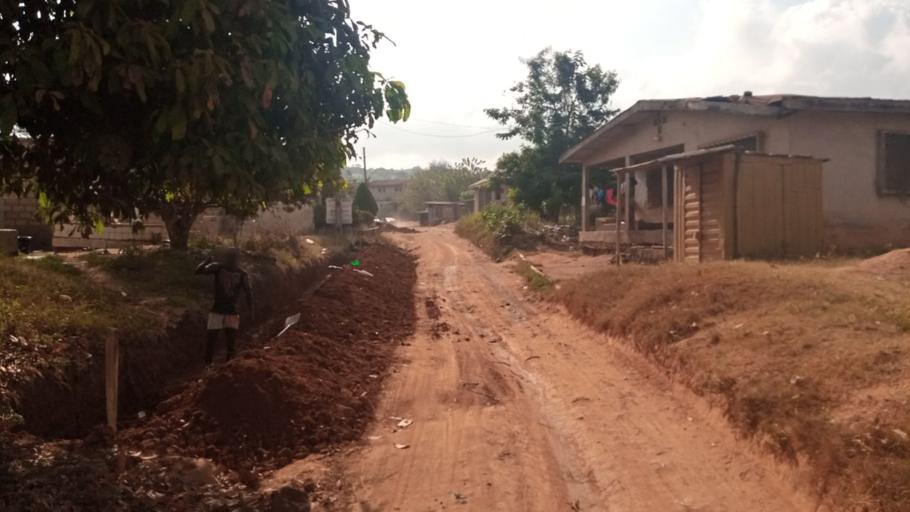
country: NG
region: Osun
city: Iragbiji
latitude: 7.9342
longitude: 4.7131
